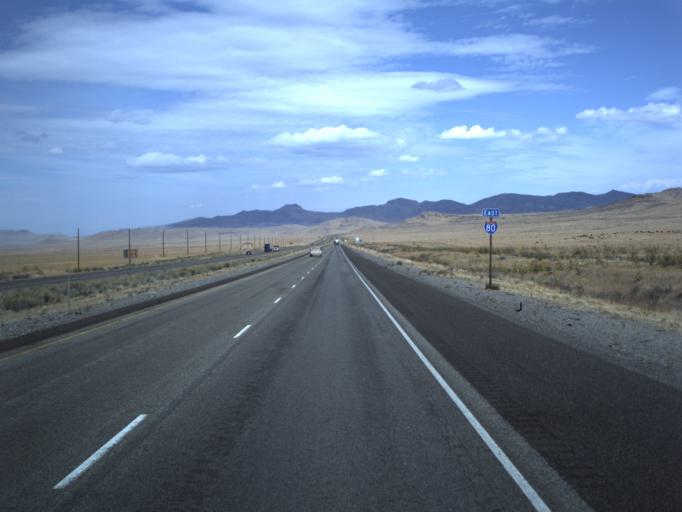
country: US
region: Utah
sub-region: Tooele County
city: Grantsville
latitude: 40.7750
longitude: -112.9749
